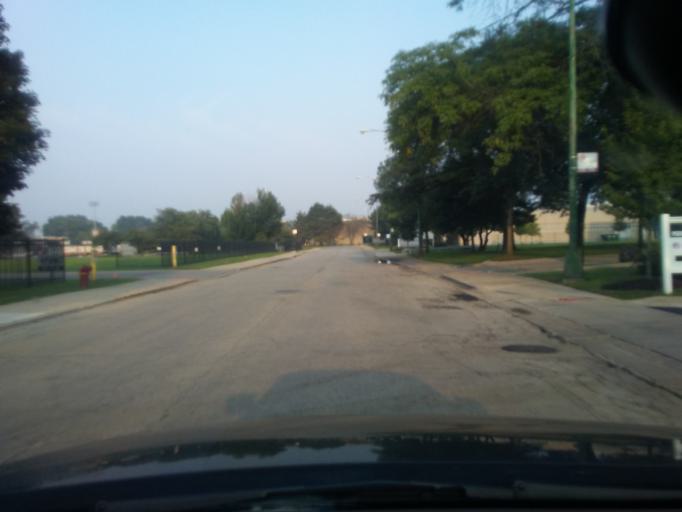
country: US
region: Illinois
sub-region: Cook County
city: Lincolnwood
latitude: 41.9495
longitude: -87.6930
